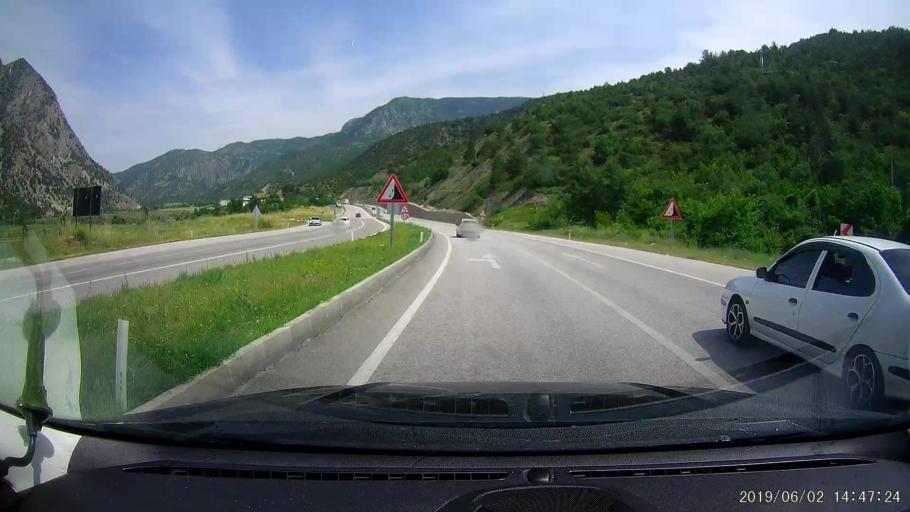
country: TR
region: Corum
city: Hacihamza
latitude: 41.0691
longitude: 34.4595
